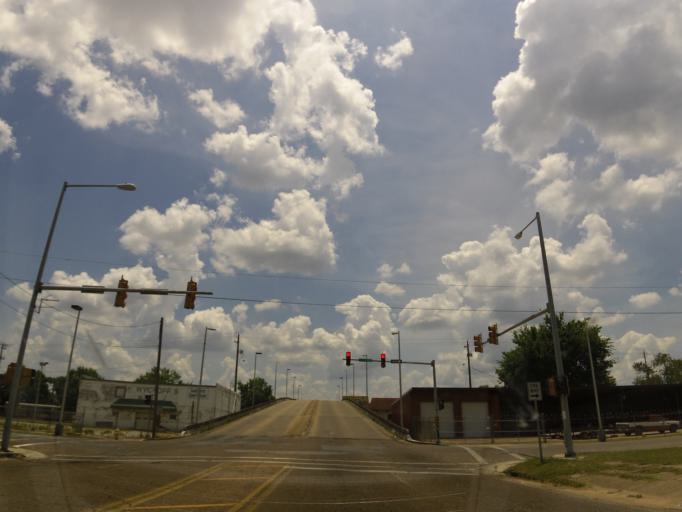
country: US
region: Mississippi
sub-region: Lauderdale County
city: Meridian
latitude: 32.3659
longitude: -88.6959
